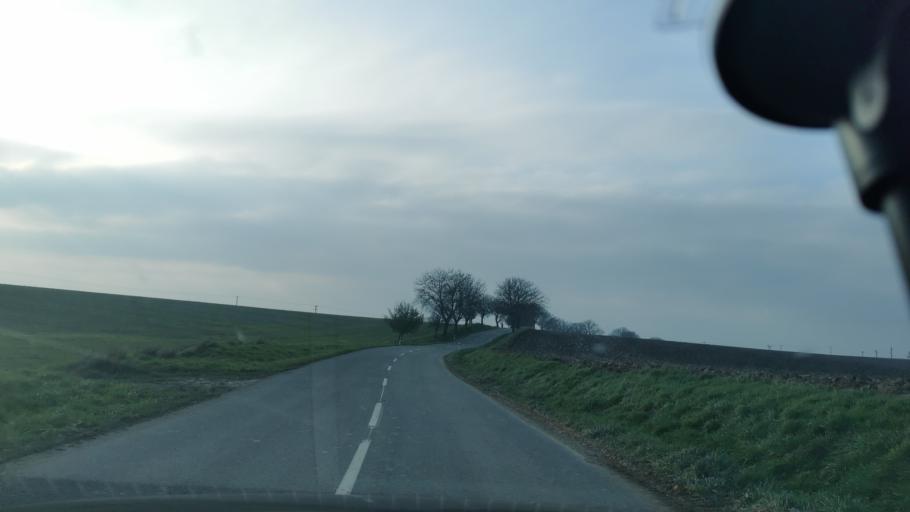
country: SK
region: Trnavsky
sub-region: Okres Skalica
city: Skalica
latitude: 48.7727
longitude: 17.2942
